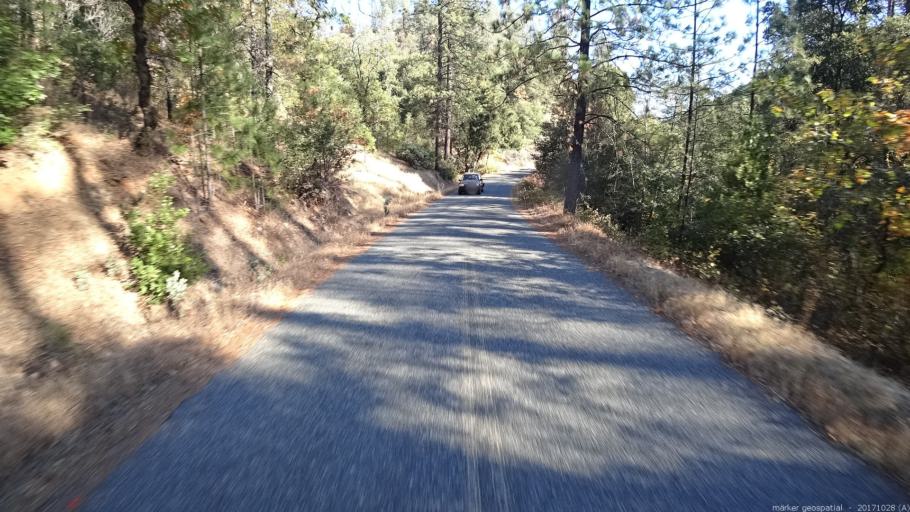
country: US
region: California
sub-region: Trinity County
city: Lewiston
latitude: 40.6537
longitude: -122.6674
